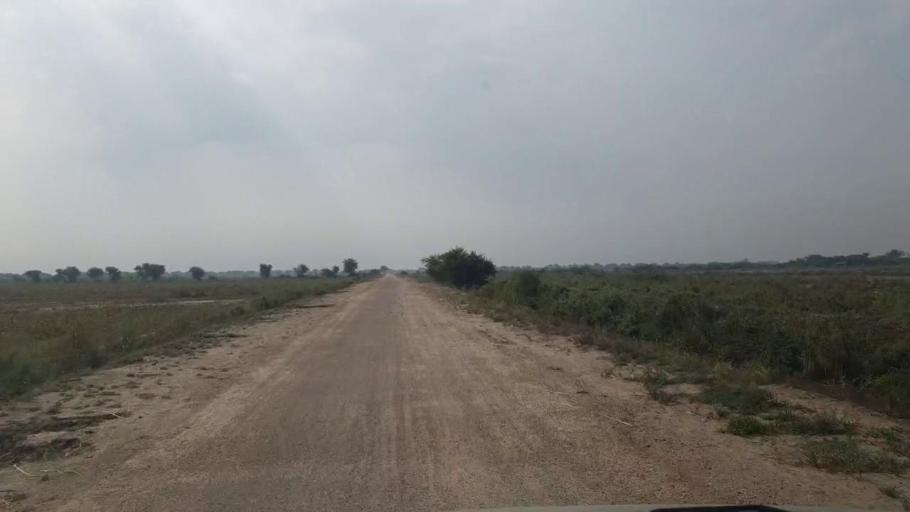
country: PK
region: Sindh
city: Talhar
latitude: 24.8707
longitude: 68.8372
